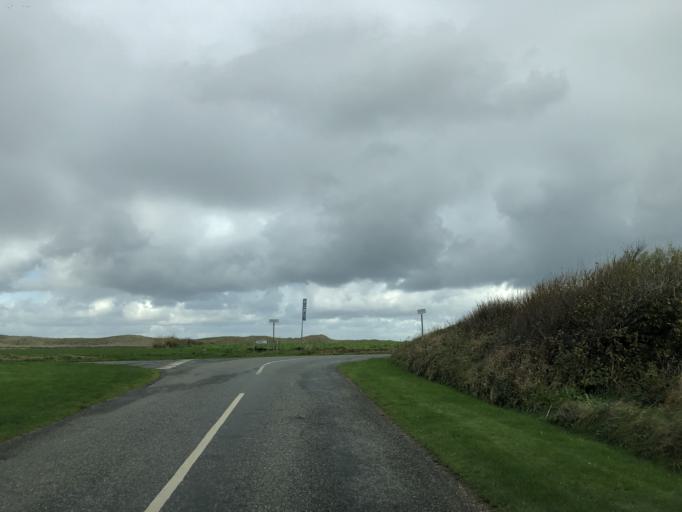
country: DK
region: Central Jutland
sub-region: Lemvig Kommune
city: Harboore
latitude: 56.4740
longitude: 8.1327
